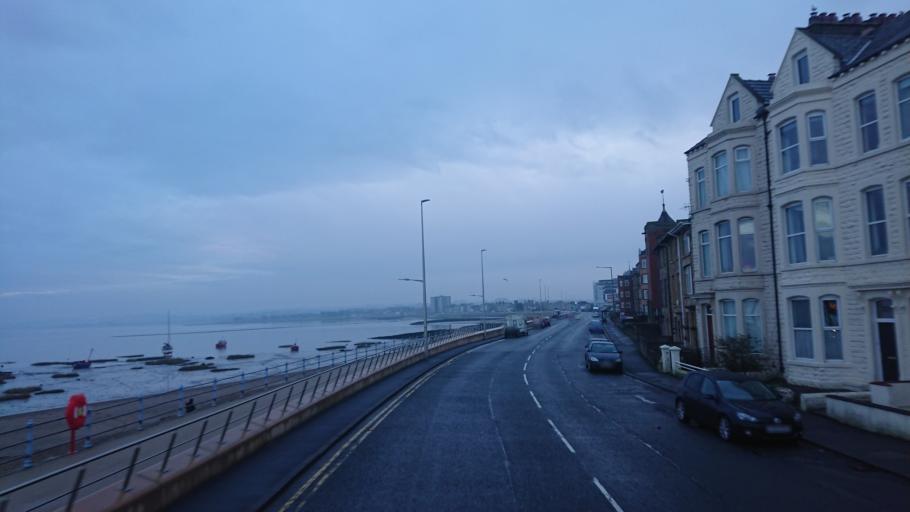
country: GB
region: England
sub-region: Lancashire
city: Morecambe
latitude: 54.0774
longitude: -2.8568
